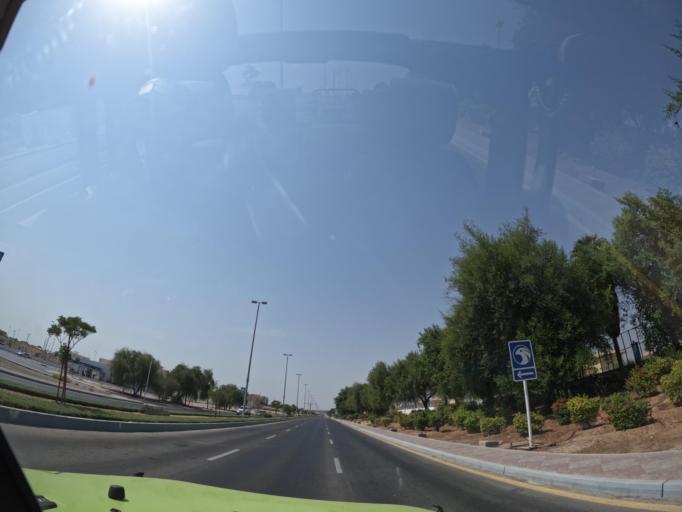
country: AE
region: Abu Dhabi
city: Abu Dhabi
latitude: 24.3047
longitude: 54.6231
